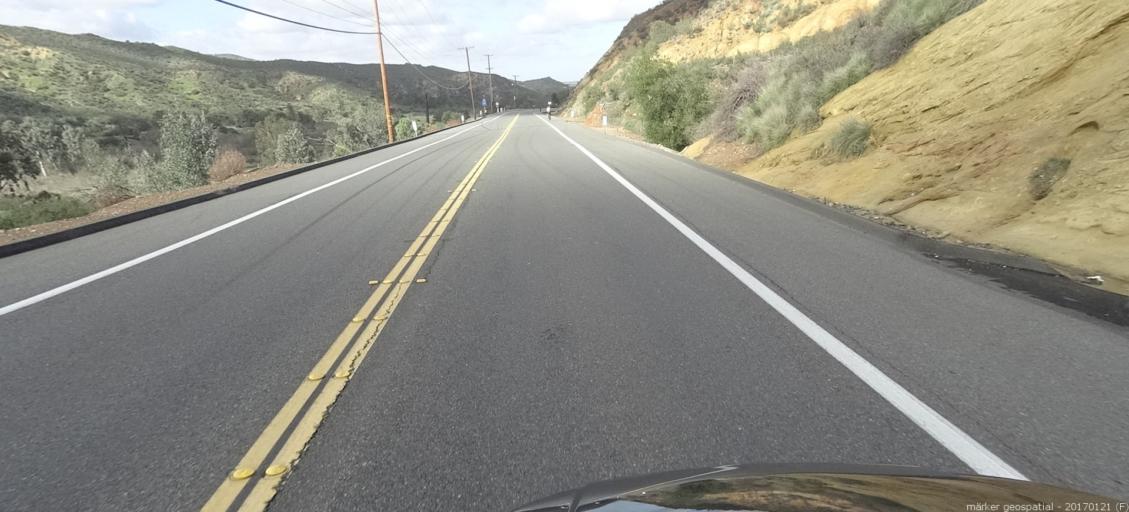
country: US
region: California
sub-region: Orange County
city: Foothill Ranch
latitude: 33.7365
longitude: -117.6582
